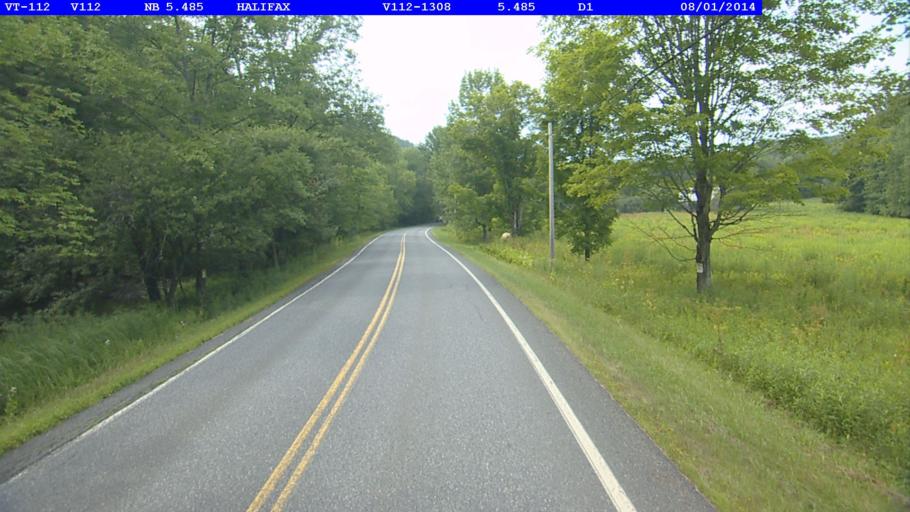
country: US
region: Massachusetts
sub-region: Franklin County
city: Colrain
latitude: 42.7743
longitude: -72.8024
